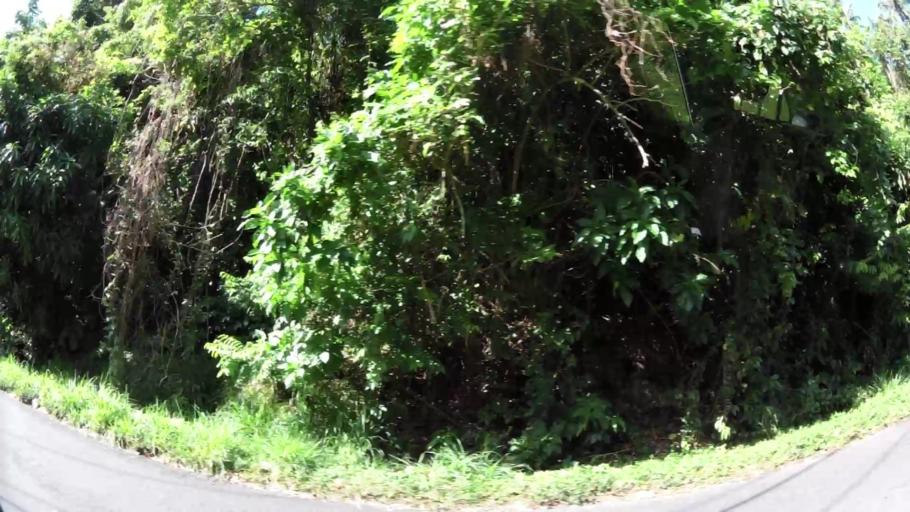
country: LC
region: Soufriere
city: Soufriere
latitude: 13.8280
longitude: -61.0493
